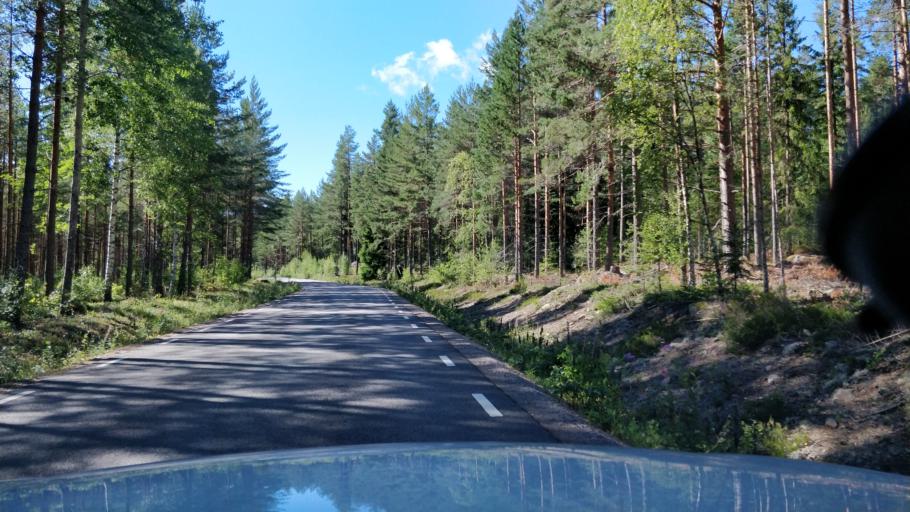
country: SE
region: Dalarna
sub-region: Faluns Kommun
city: Bjursas
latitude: 60.7525
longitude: 15.4912
